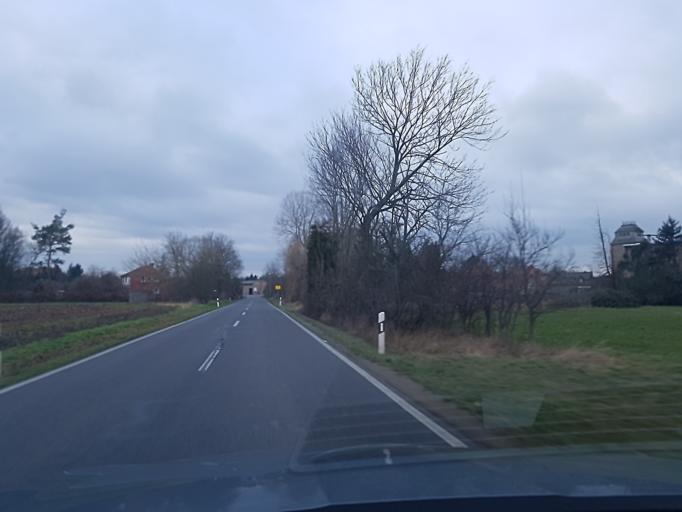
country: DE
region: Brandenburg
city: Sonnewalde
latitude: 51.6958
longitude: 13.6546
